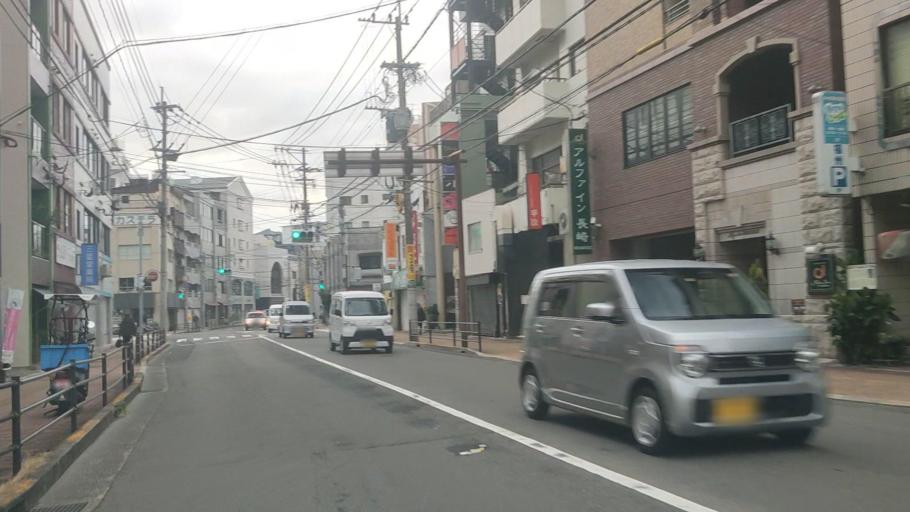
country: JP
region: Nagasaki
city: Nagasaki-shi
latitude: 32.7694
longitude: 129.8664
